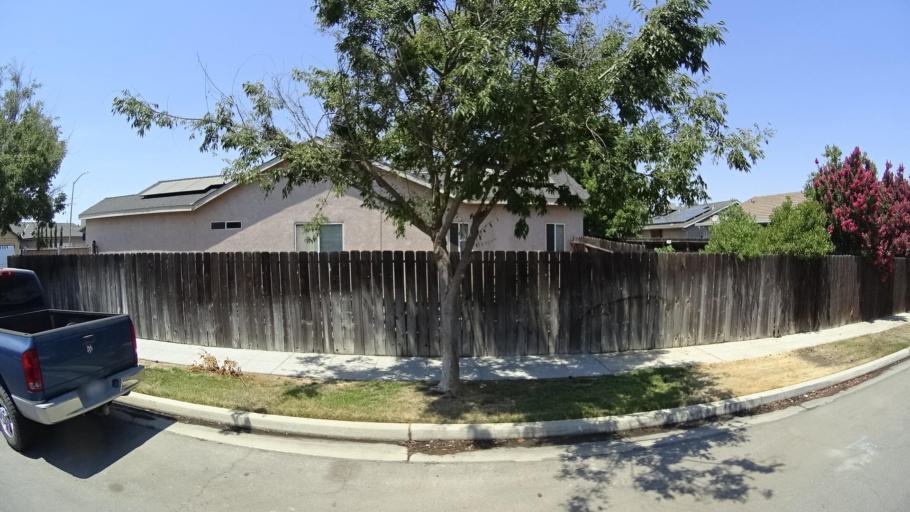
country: US
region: California
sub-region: Fresno County
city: Sunnyside
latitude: 36.7423
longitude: -119.6715
